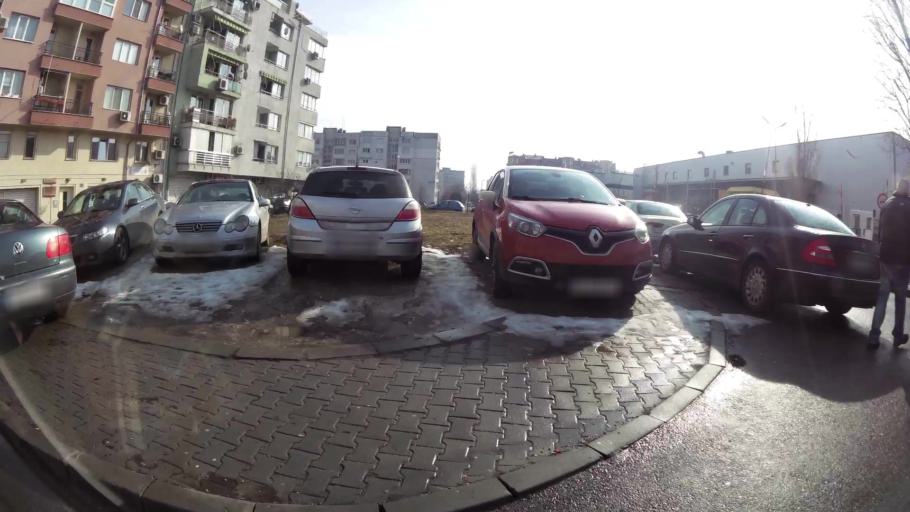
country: BG
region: Sofiya
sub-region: Obshtina Bozhurishte
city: Bozhurishte
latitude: 42.7206
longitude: 23.2565
